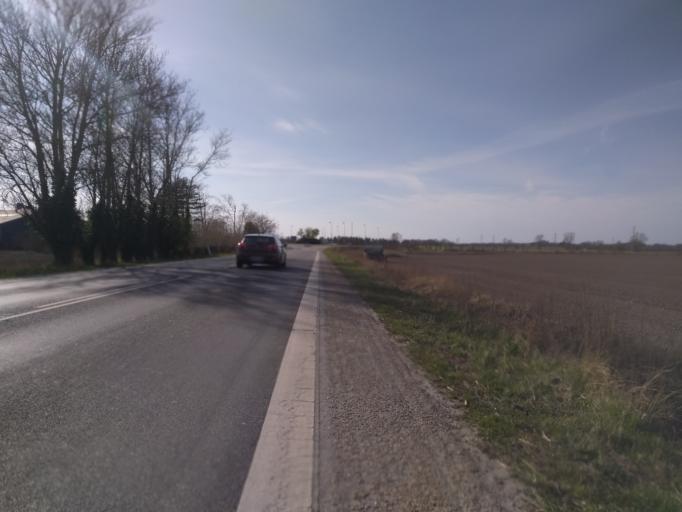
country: DK
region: South Denmark
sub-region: Odense Kommune
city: Bullerup
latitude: 55.3887
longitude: 10.4827
